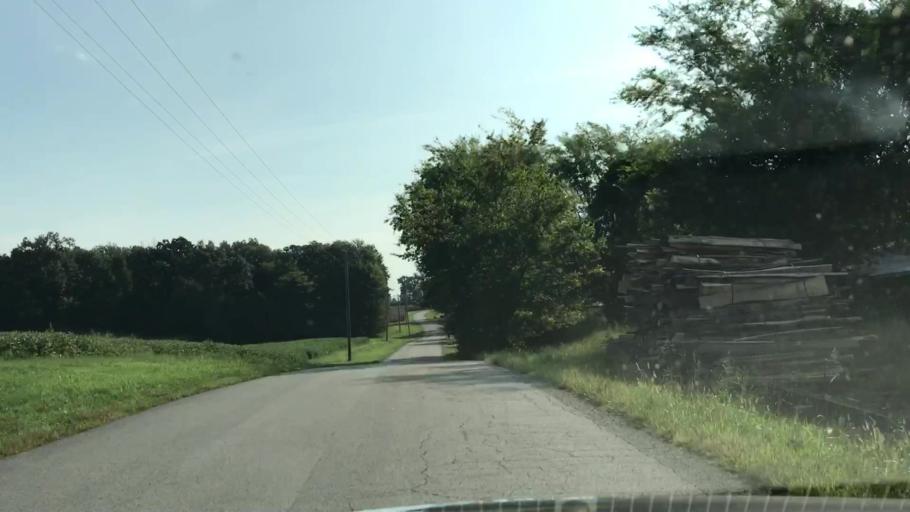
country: US
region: Kentucky
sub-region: Todd County
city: Elkton
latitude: 36.7664
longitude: -87.1639
